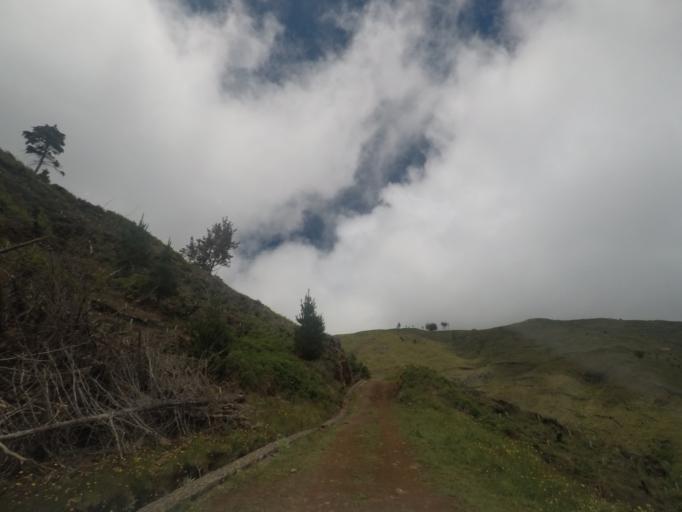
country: PT
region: Madeira
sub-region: Funchal
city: Nossa Senhora do Monte
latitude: 32.7044
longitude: -16.9046
